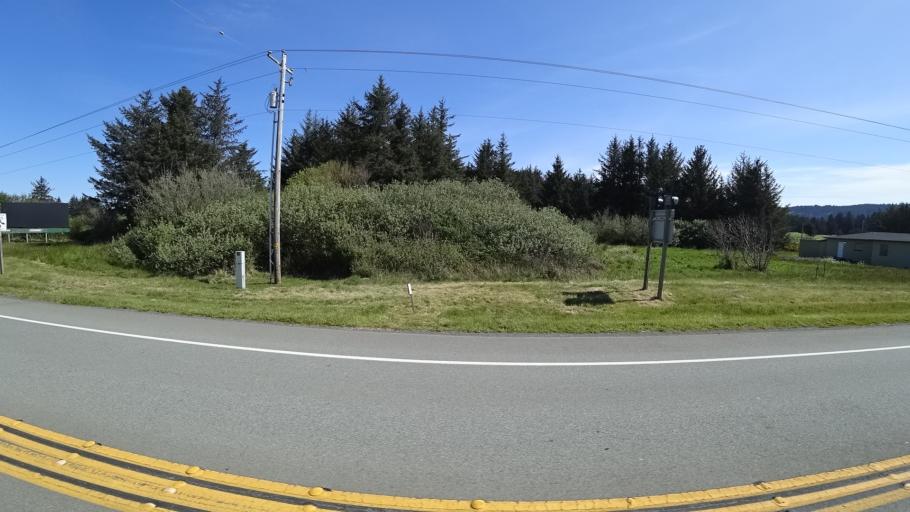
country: US
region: California
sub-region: Del Norte County
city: Bertsch-Oceanview
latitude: 41.7456
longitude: -124.1758
